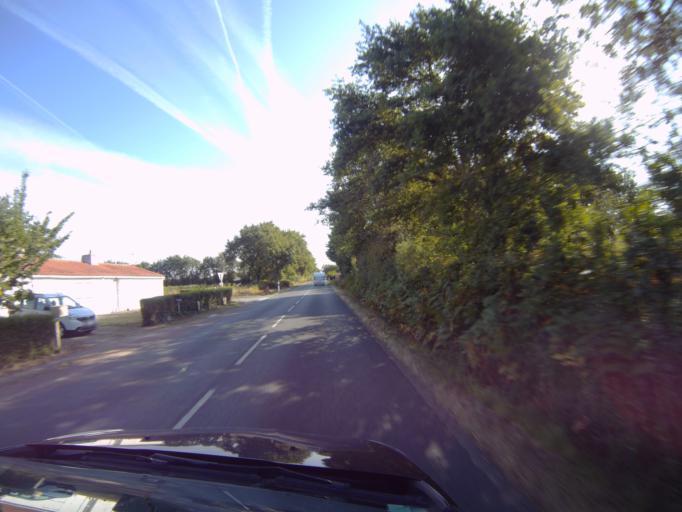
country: FR
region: Pays de la Loire
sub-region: Departement de la Vendee
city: Saint-Hilaire-de-Talmont
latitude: 46.5106
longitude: -1.5665
